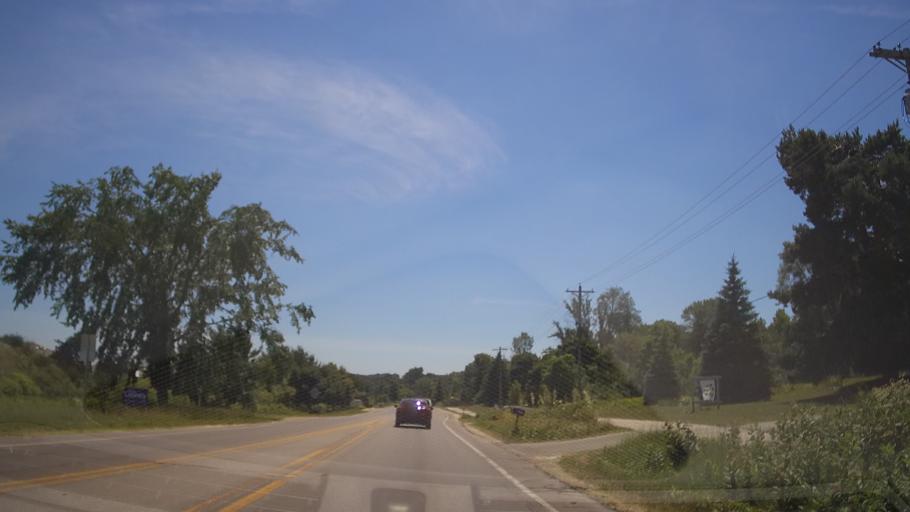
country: US
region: Michigan
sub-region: Grand Traverse County
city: Traverse City
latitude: 44.7398
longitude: -85.6558
